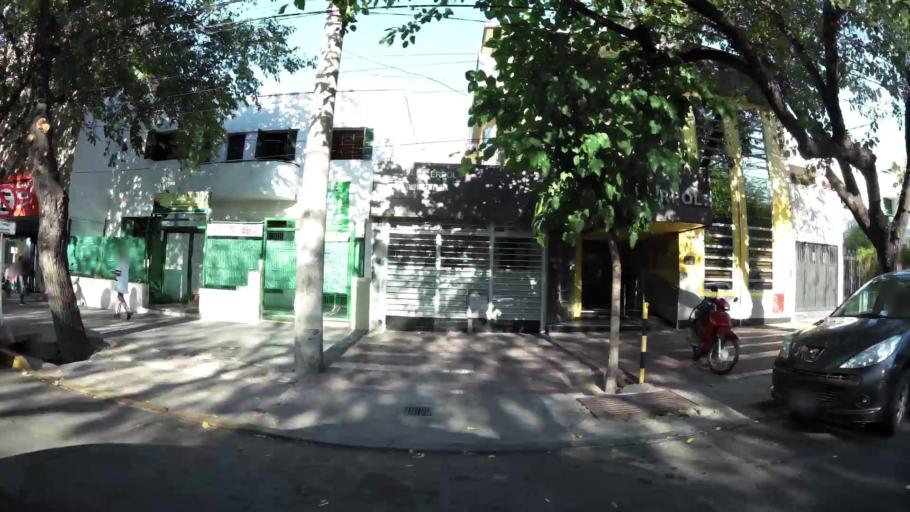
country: AR
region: Mendoza
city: Mendoza
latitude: -32.9060
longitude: -68.8433
